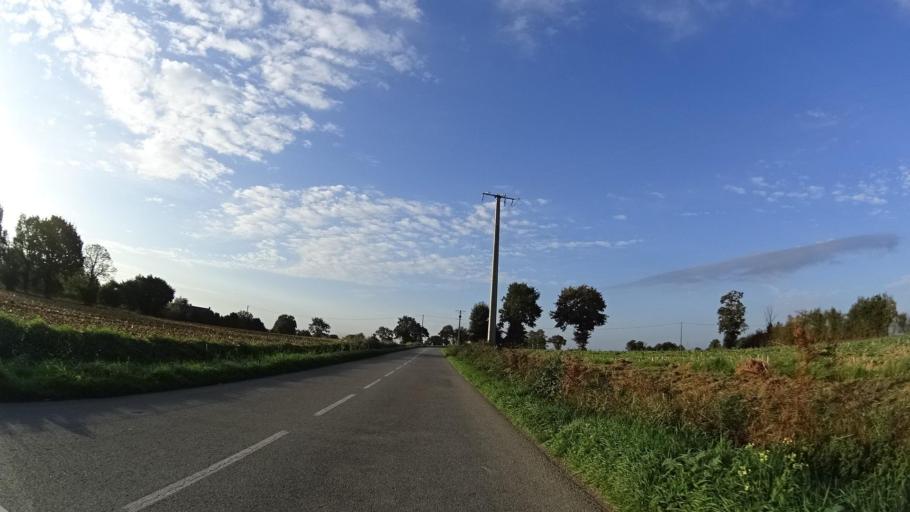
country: FR
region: Brittany
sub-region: Departement des Cotes-d'Armor
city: Plouasne
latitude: 48.2869
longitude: -1.9693
